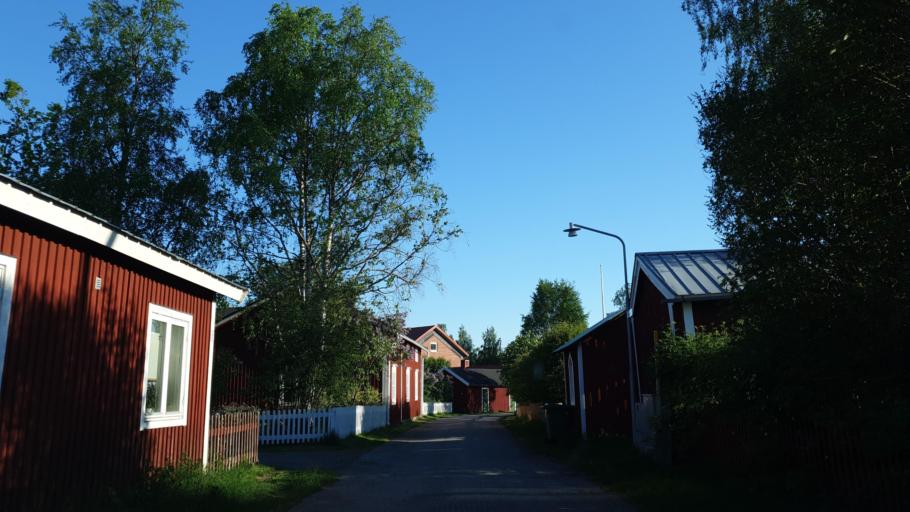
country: SE
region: Norrbotten
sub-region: Lulea Kommun
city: Gammelstad
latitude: 65.6452
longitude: 22.0324
